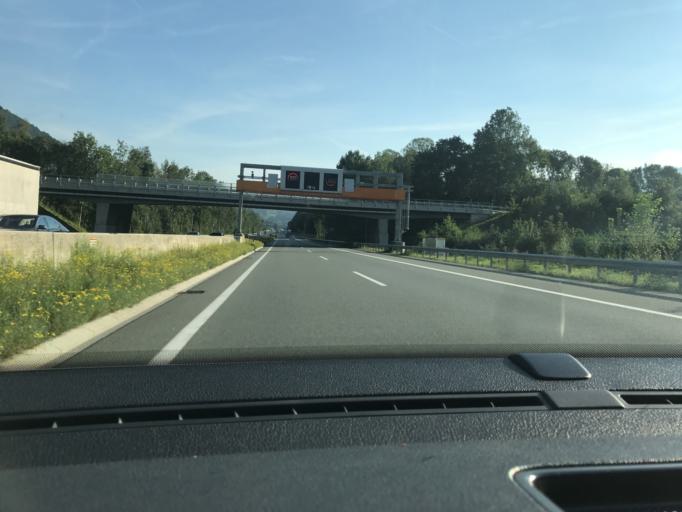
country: AT
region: Tyrol
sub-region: Politischer Bezirk Kufstein
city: Schwoich
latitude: 47.5685
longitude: 12.1415
